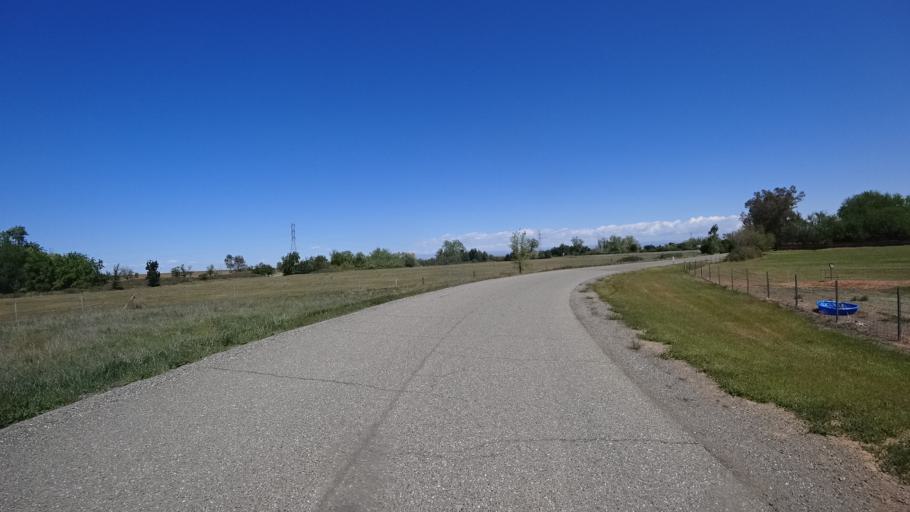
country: US
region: California
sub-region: Glenn County
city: Orland
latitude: 39.7980
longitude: -122.2041
